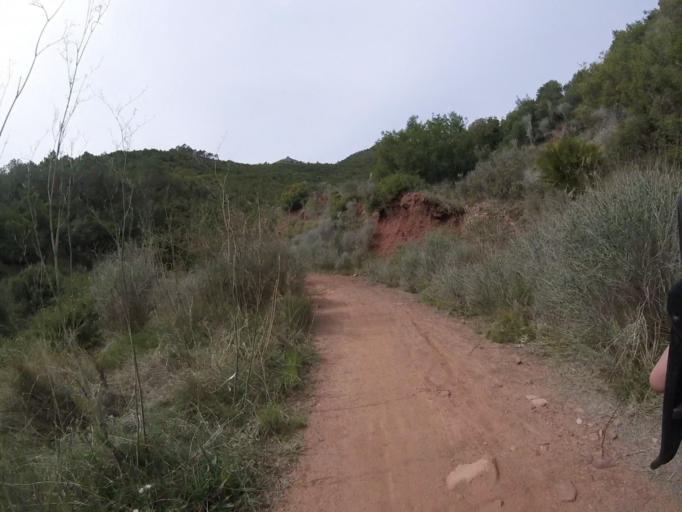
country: ES
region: Valencia
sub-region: Provincia de Castello
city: Benicassim
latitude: 40.0702
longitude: 0.0372
